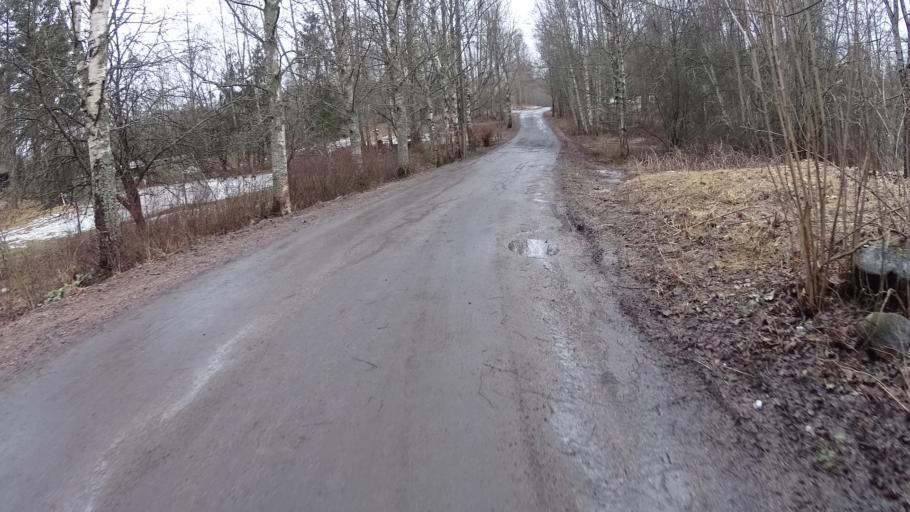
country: FI
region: Uusimaa
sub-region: Helsinki
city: Kilo
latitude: 60.2613
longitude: 24.7926
